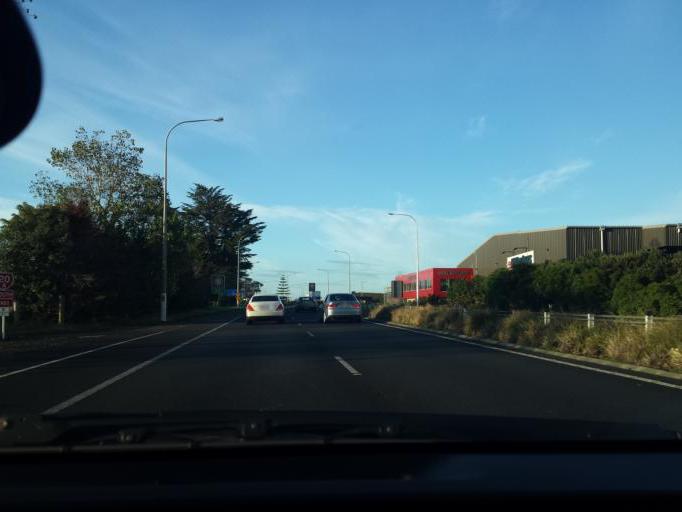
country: NZ
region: Auckland
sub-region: Auckland
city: Mangere
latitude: -36.9883
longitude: 174.7859
